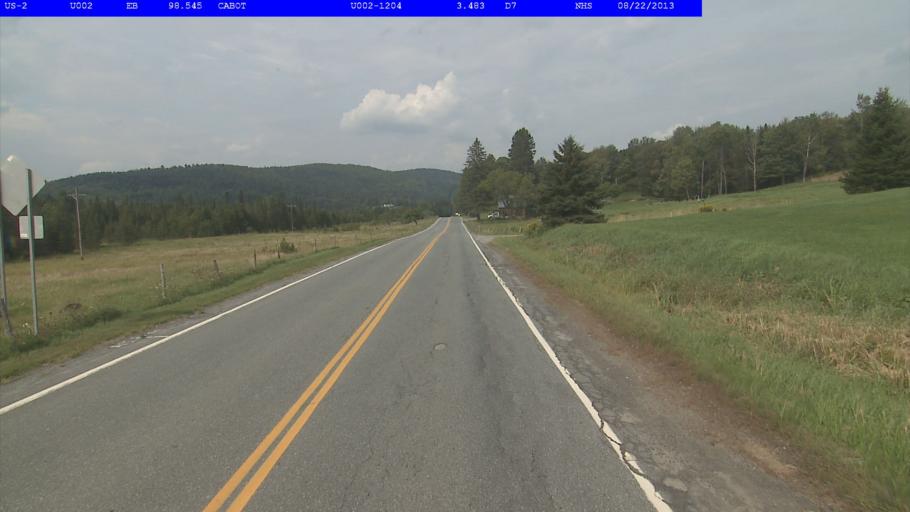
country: US
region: Vermont
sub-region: Caledonia County
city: Hardwick
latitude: 44.3751
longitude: -72.2604
